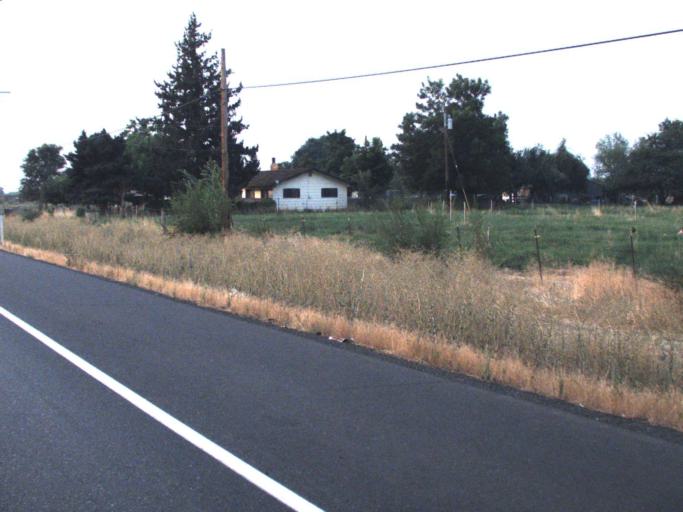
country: US
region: Washington
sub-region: Yakima County
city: Wapato
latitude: 46.4724
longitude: -120.4429
